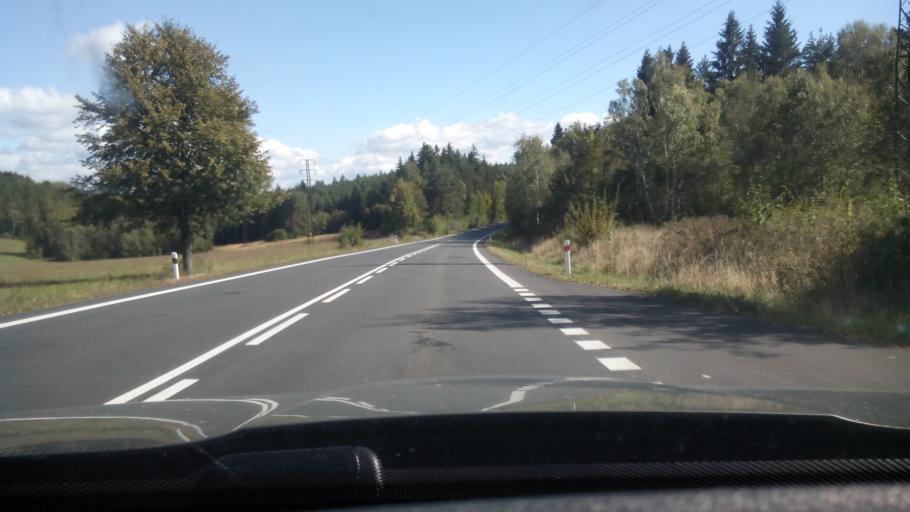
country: CZ
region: Jihocesky
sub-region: Okres Prachatice
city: Zdikov
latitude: 49.0674
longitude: 13.7244
